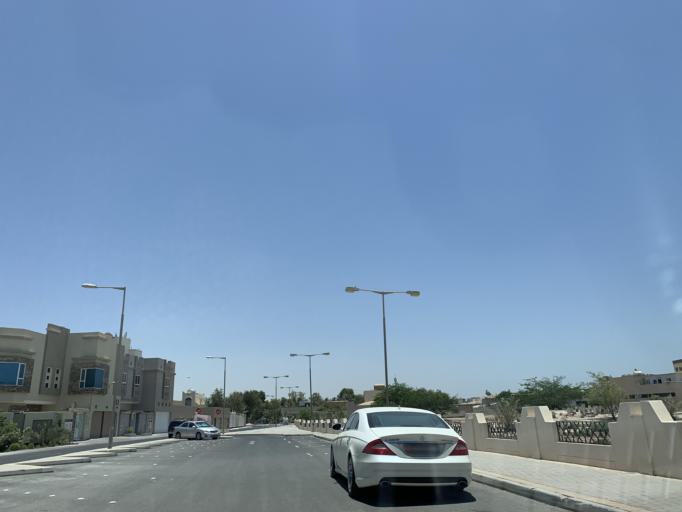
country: BH
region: Manama
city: Jidd Hafs
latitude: 26.2294
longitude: 50.4843
